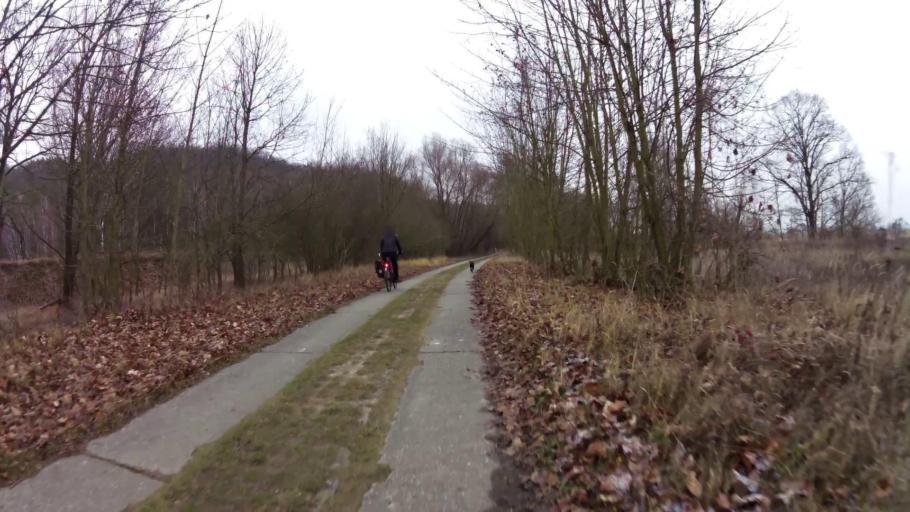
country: PL
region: West Pomeranian Voivodeship
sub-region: Powiat gryfinski
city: Cedynia
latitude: 52.9317
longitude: 14.1501
